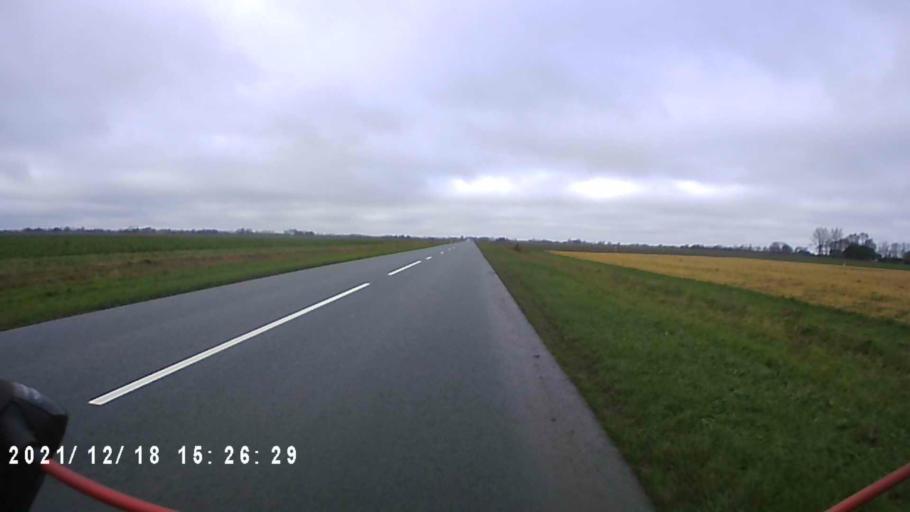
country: NL
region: Friesland
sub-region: Gemeente Kollumerland en Nieuwkruisland
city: Kollum
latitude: 53.3271
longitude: 6.1497
